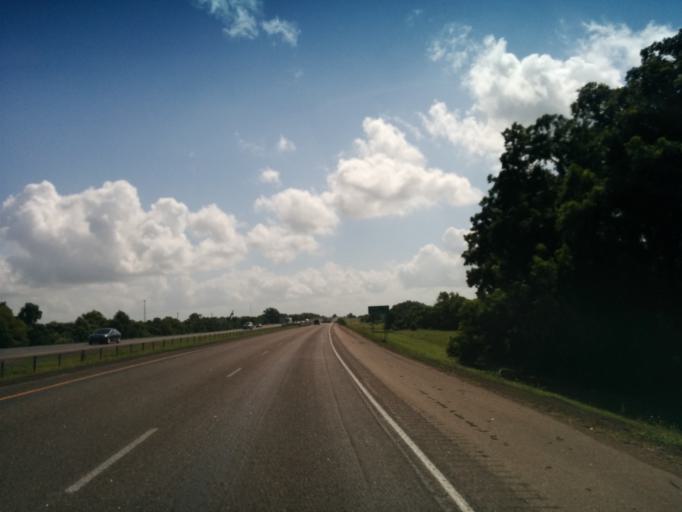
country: US
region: Texas
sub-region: Colorado County
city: Columbus
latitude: 29.6989
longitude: -96.5282
